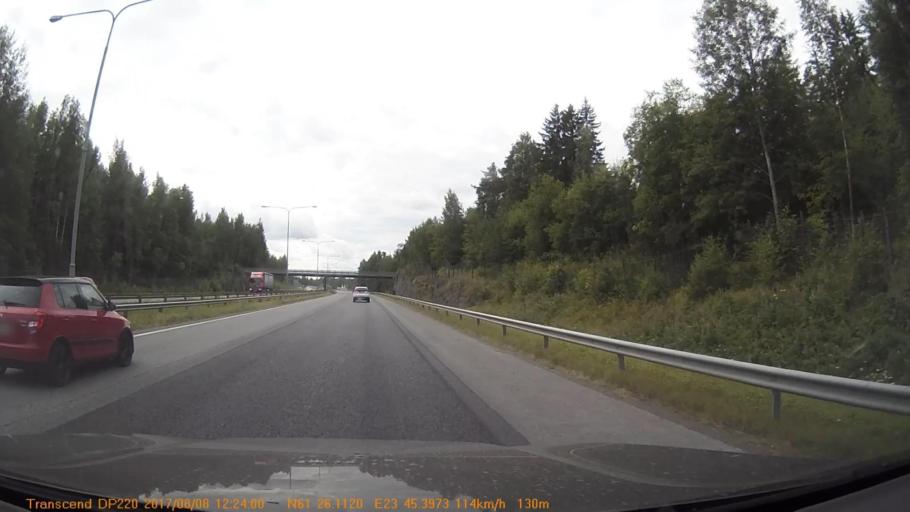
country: FI
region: Pirkanmaa
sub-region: Tampere
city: Tampere
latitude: 61.4351
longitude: 23.7564
